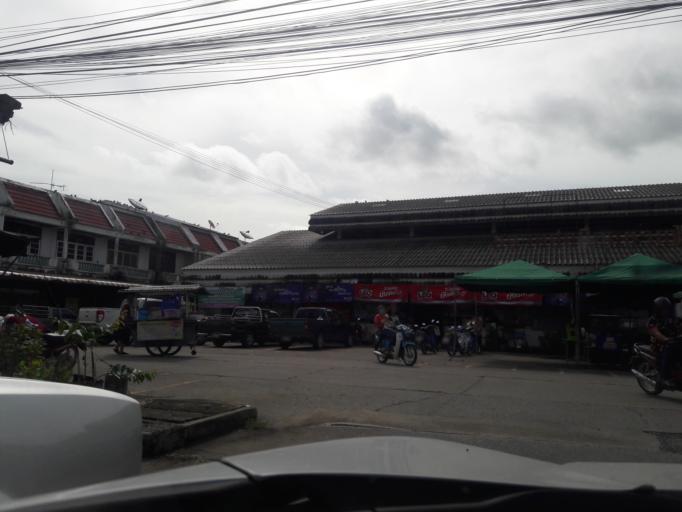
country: TH
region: Nakhon Sawan
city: Tak Fa
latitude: 15.3461
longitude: 100.4955
